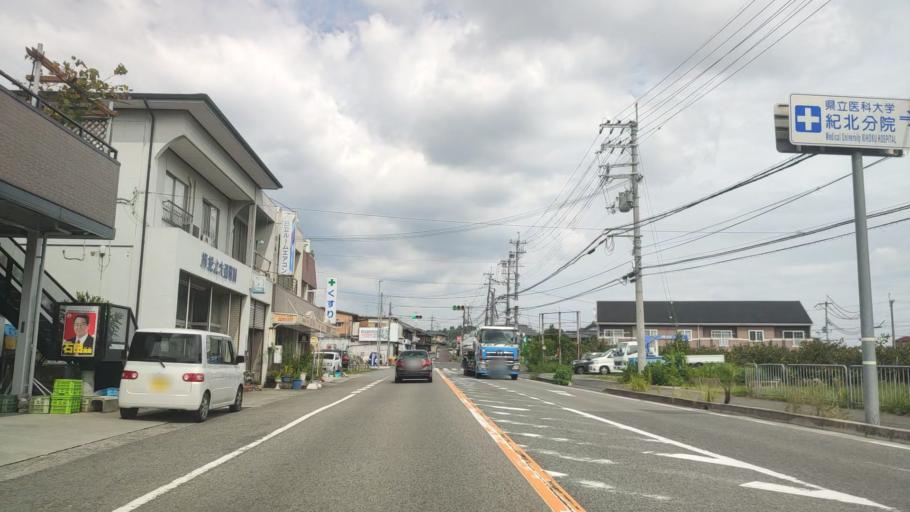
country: JP
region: Wakayama
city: Hashimoto
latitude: 34.3025
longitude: 135.5296
